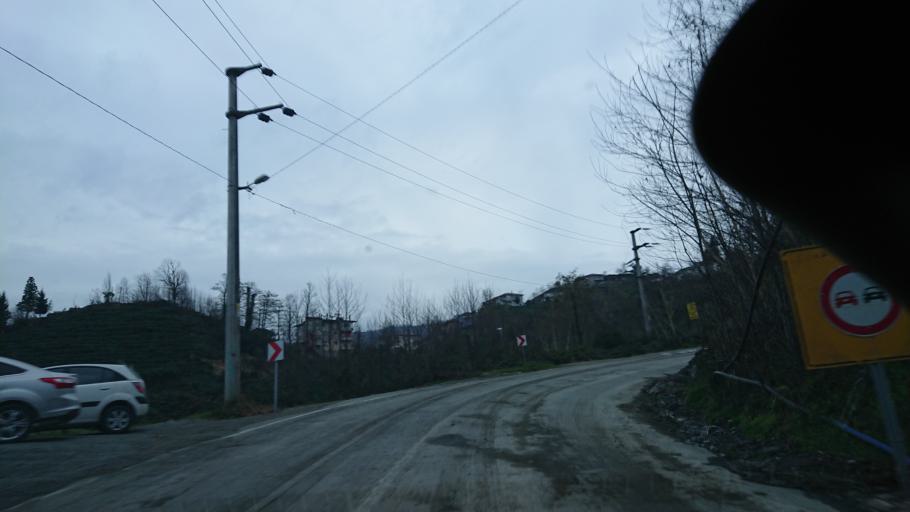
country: TR
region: Rize
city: Rize
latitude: 41.0177
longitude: 40.4988
